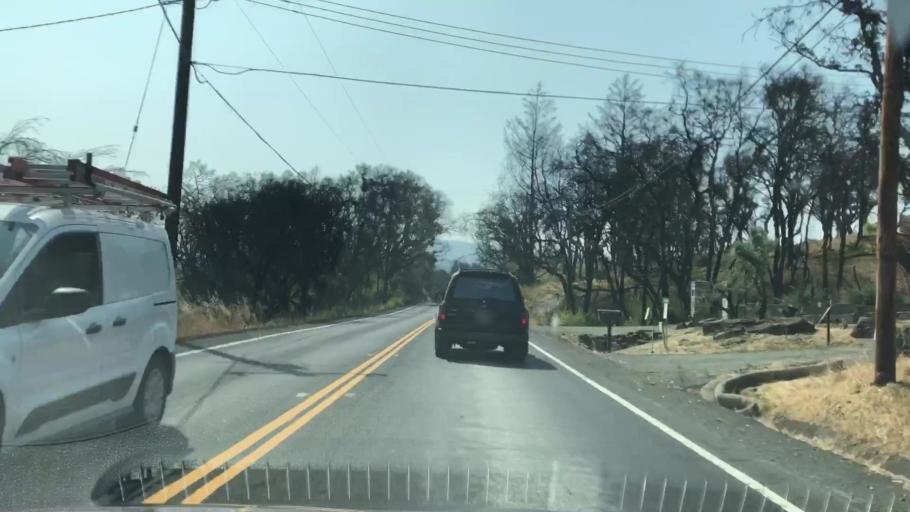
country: US
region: California
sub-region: Sonoma County
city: Larkfield-Wikiup
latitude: 38.5164
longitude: -122.7200
